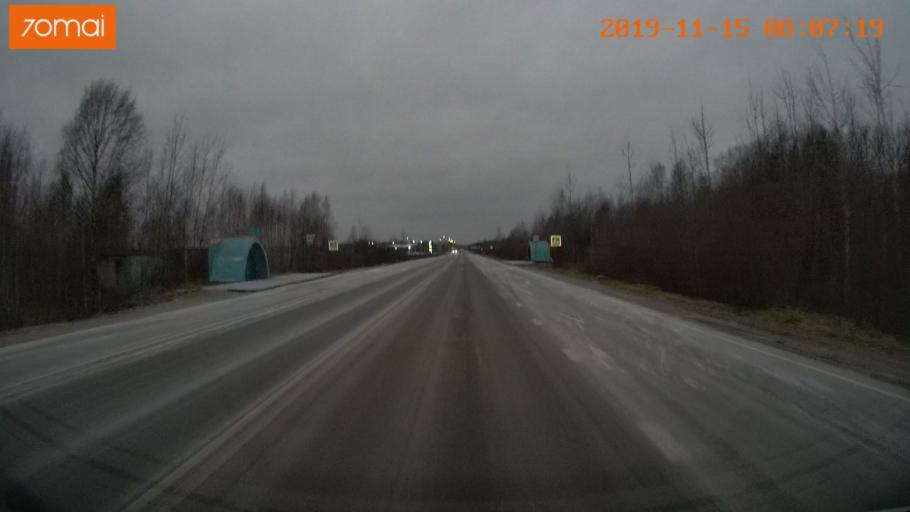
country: RU
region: Vologda
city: Cherepovets
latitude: 59.0260
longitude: 38.0191
